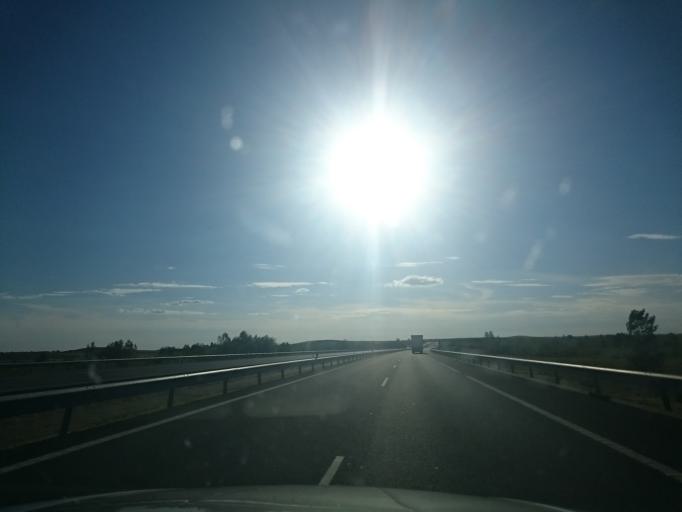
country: ES
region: Castille and Leon
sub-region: Provincia de Burgos
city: Villasandino
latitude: 42.3943
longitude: -4.1041
